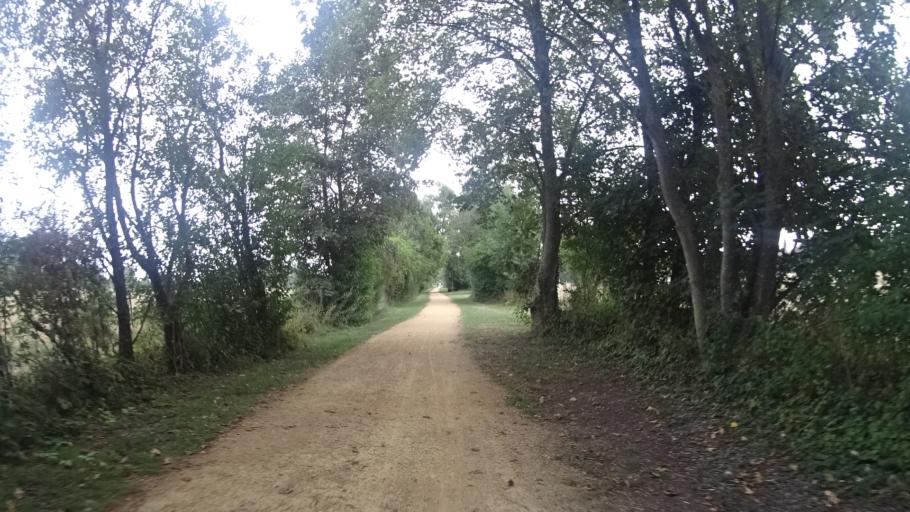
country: FR
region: Picardie
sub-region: Departement de l'Aisne
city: Origny-Sainte-Benoite
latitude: 49.8444
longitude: 3.4916
